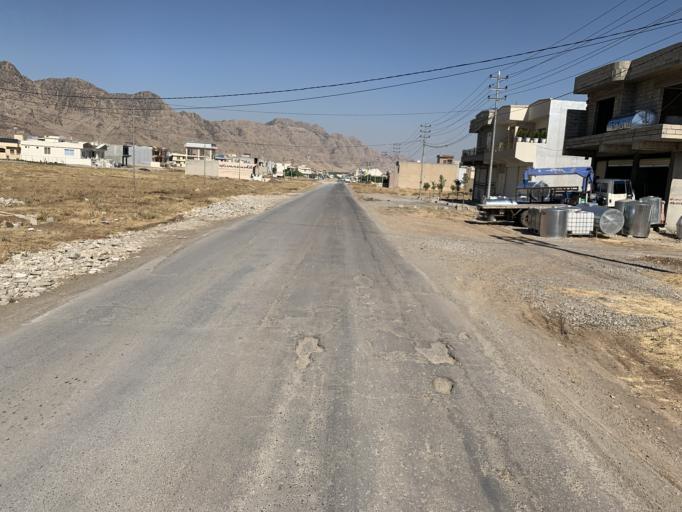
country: IQ
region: As Sulaymaniyah
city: Raniye
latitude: 36.2602
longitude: 44.8593
